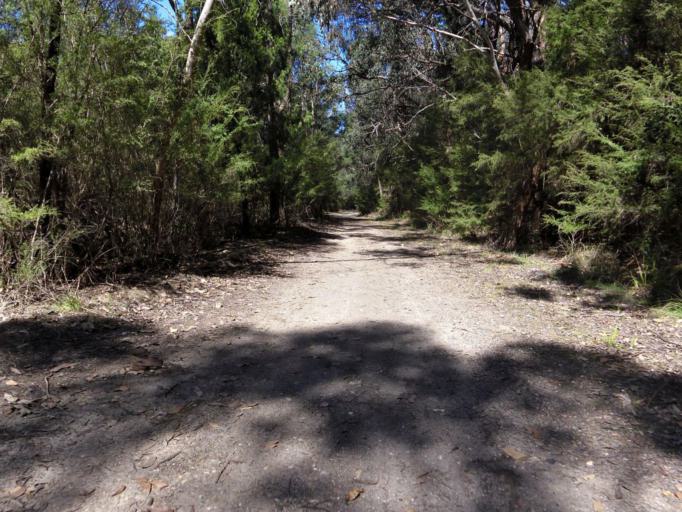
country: AU
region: Victoria
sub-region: Latrobe
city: Moe
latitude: -38.1707
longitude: 146.3309
